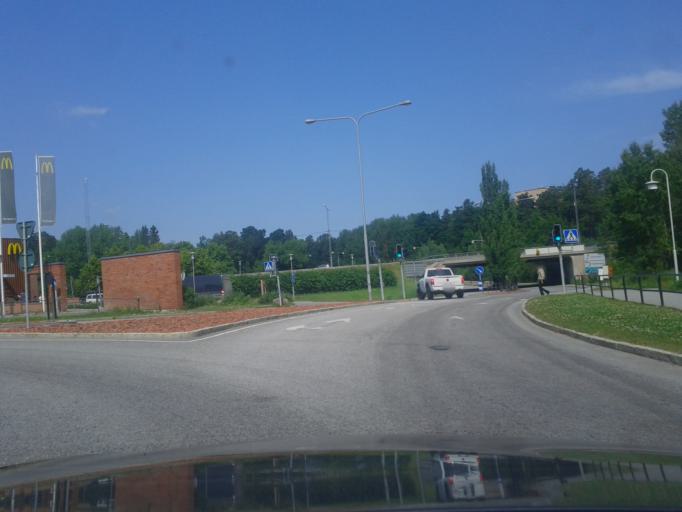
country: SE
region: Stockholm
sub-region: Taby Kommun
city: Taby
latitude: 59.4453
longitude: 18.1226
